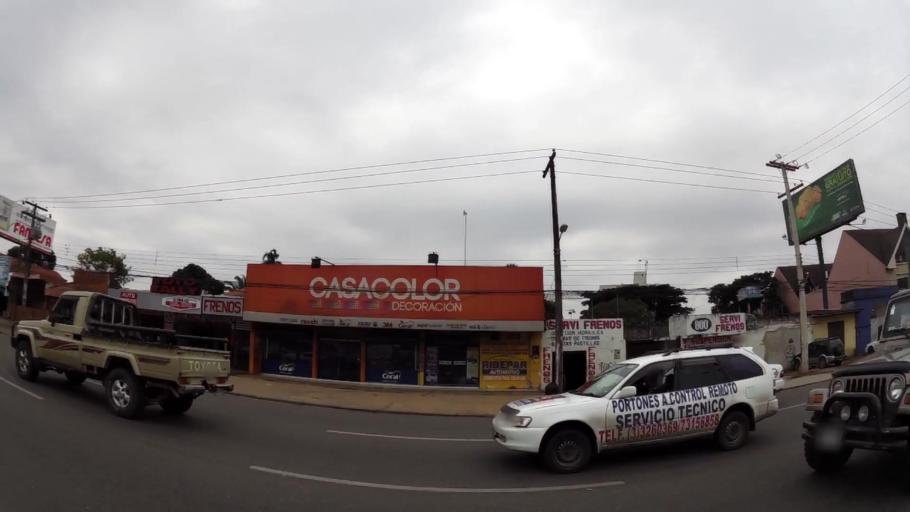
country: BO
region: Santa Cruz
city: Santa Cruz de la Sierra
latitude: -17.7736
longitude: -63.1659
